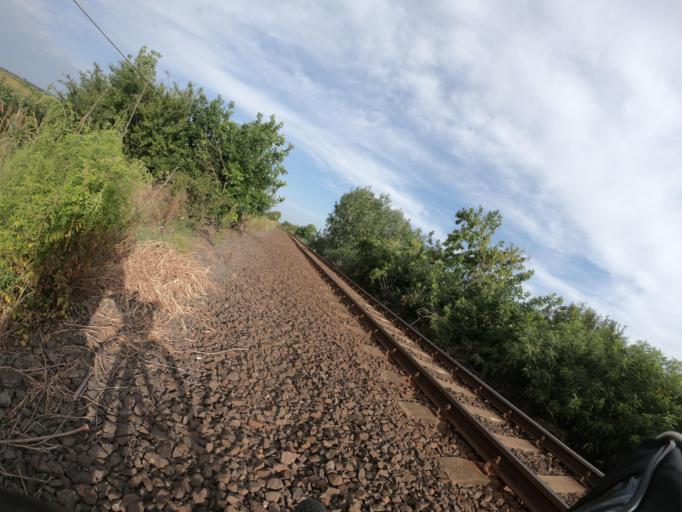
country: HU
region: Hajdu-Bihar
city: Hortobagy
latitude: 47.6086
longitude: 21.0507
